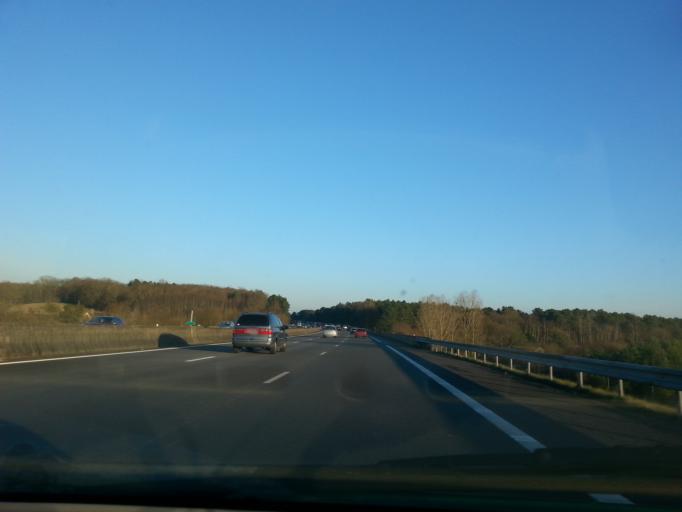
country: FR
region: Pays de la Loire
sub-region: Departement de la Sarthe
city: Connerre
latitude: 48.0750
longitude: 0.4694
